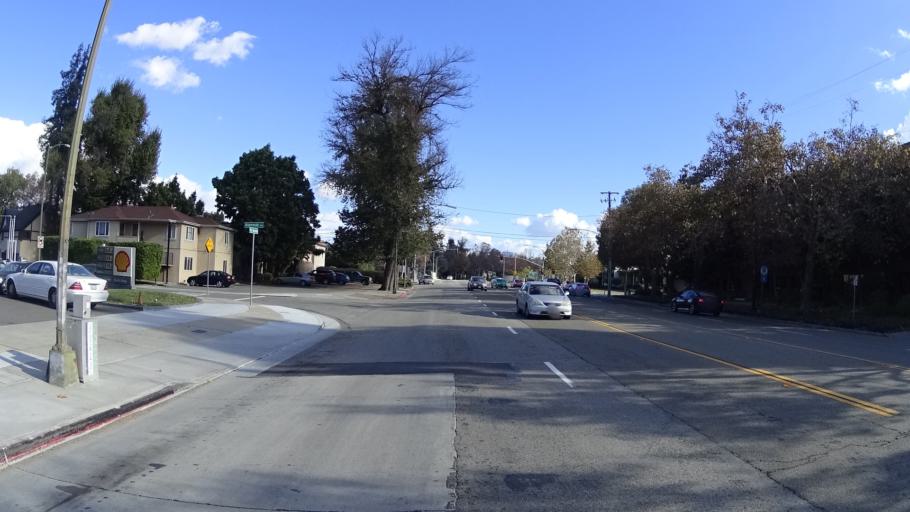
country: US
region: California
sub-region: Santa Clara County
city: Burbank
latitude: 37.3434
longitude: -121.9282
